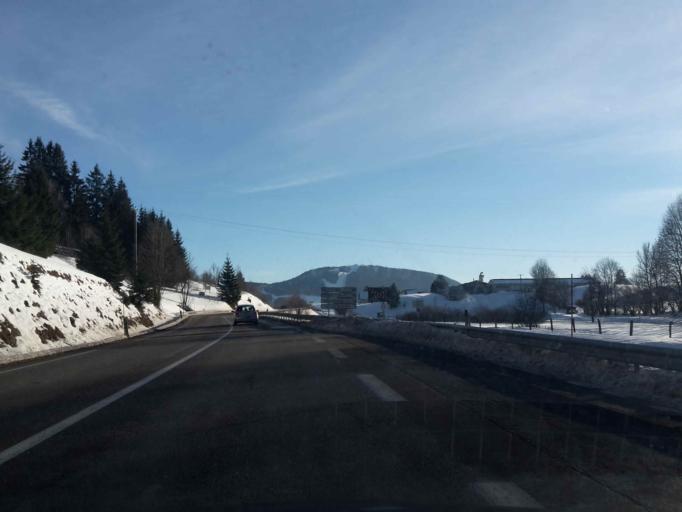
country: FR
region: Franche-Comte
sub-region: Departement du Doubs
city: Jougne
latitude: 46.7980
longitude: 6.3562
